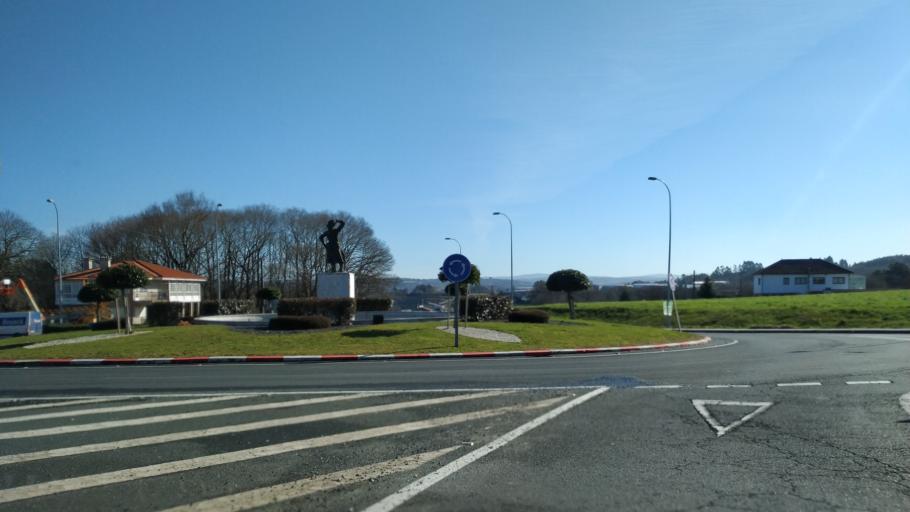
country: ES
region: Galicia
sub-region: Provincia de Pontevedra
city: Silleda
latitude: 42.6956
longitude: -8.2405
